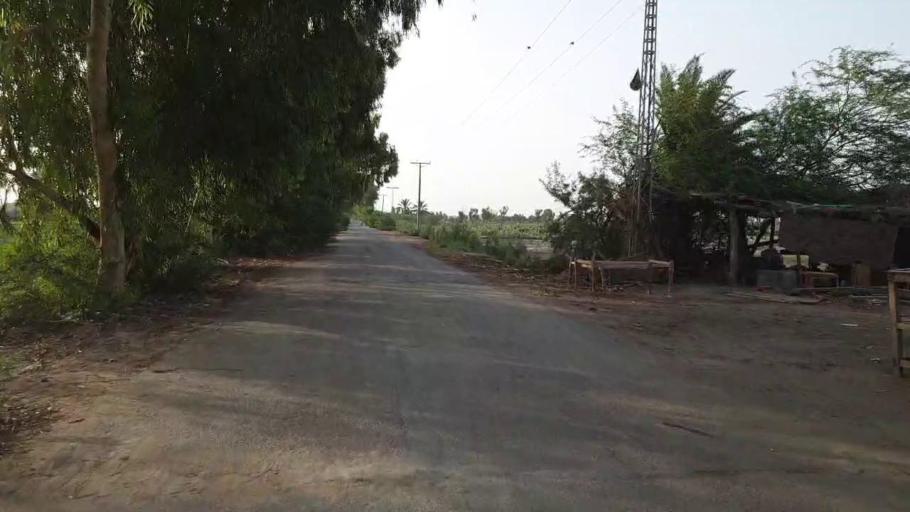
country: PK
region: Sindh
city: Bozdar
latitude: 27.1112
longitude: 68.9594
